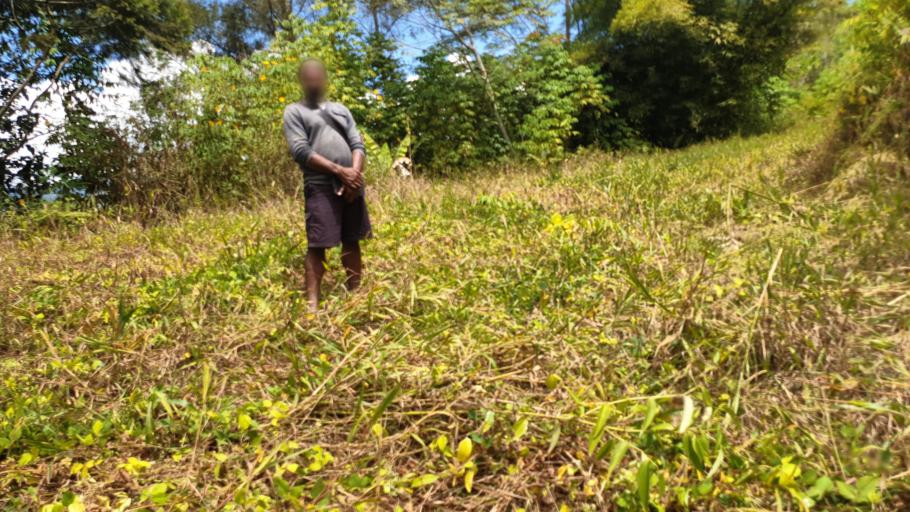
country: PG
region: Jiwaka
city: Minj
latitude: -5.9146
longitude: 144.8265
